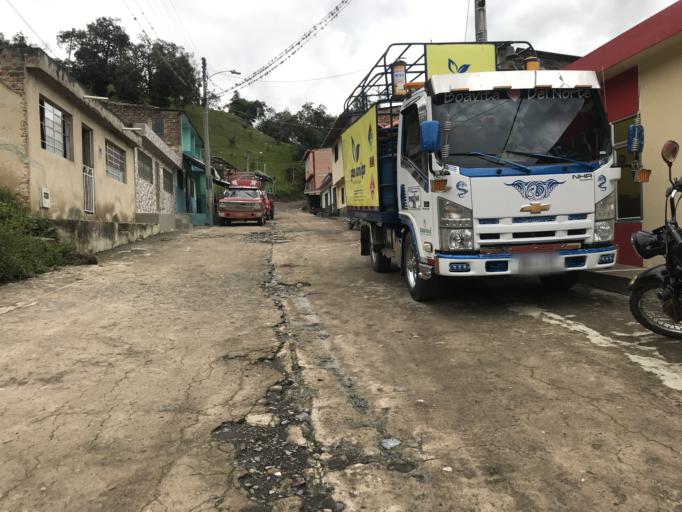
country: CO
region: Boyaca
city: Boavita
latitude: 6.3307
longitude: -72.5833
